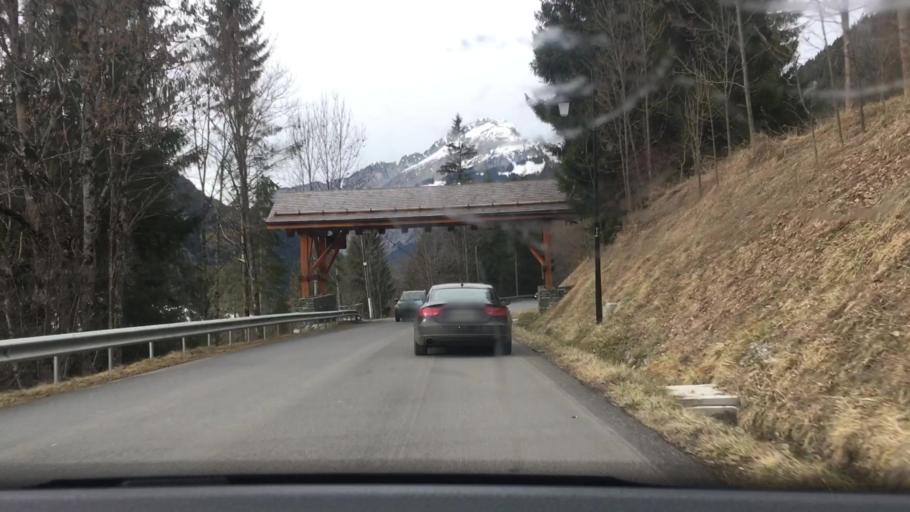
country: FR
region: Rhone-Alpes
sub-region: Departement de la Haute-Savoie
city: Chatel
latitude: 46.2763
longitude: 6.8310
